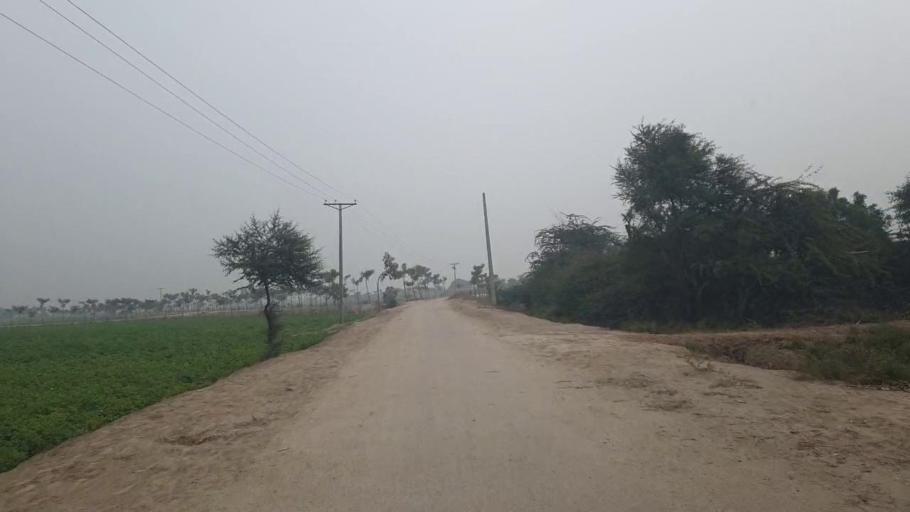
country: PK
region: Sindh
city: Tando Adam
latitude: 25.7477
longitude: 68.6736
